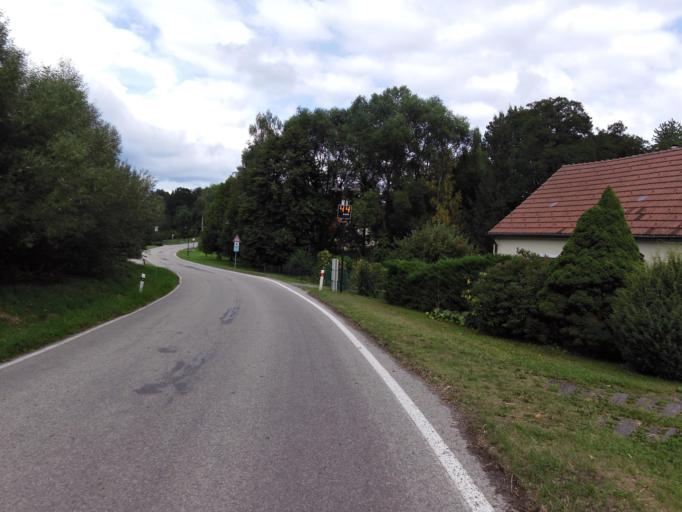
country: CZ
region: Jihocesky
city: Horni Stropnice
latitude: 48.7688
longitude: 14.7551
